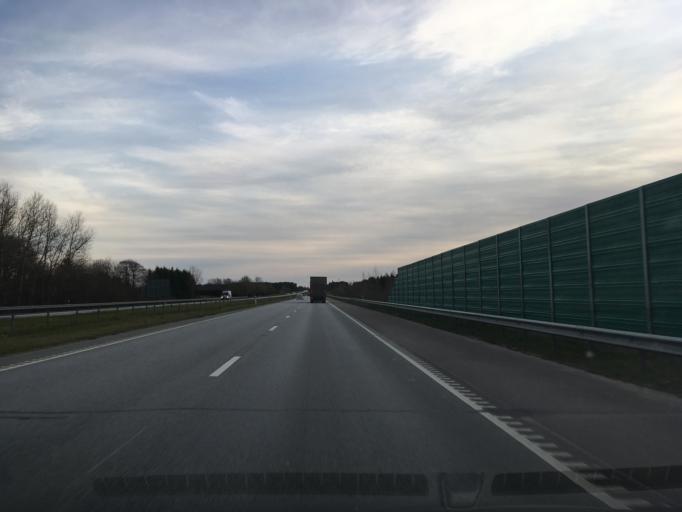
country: EE
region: Harju
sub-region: Kuusalu vald
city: Kuusalu
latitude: 59.4457
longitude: 25.3882
